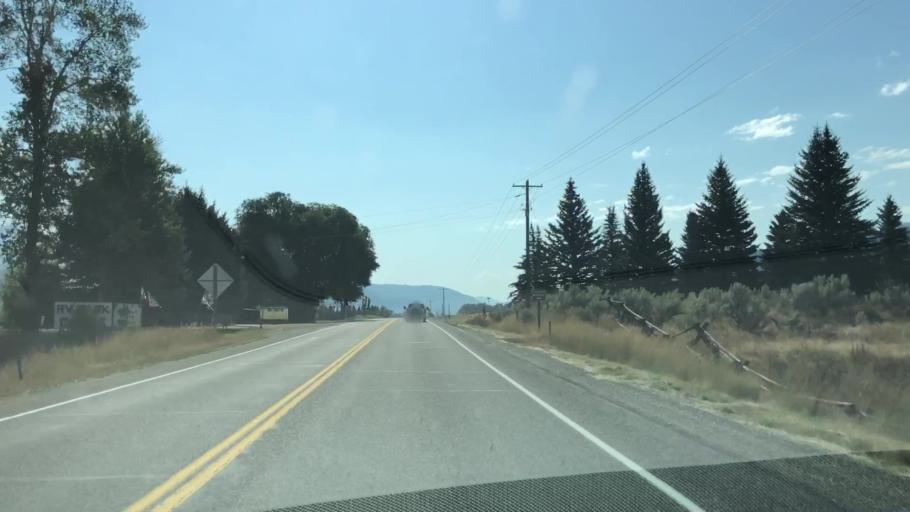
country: US
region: Idaho
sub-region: Teton County
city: Victor
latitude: 43.4010
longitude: -111.2873
